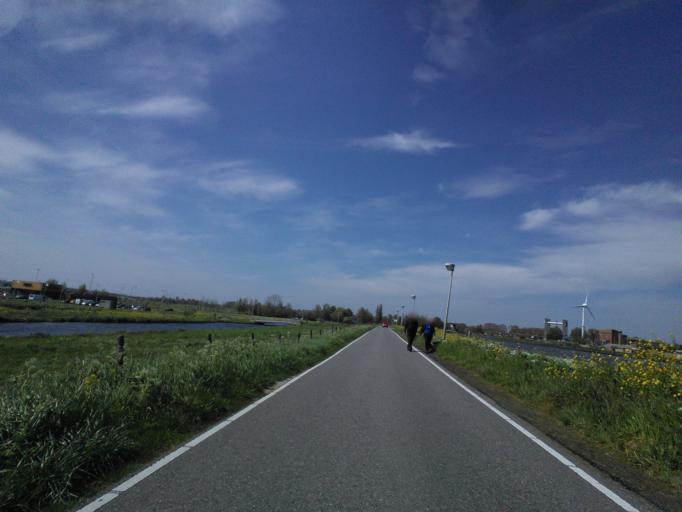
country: NL
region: South Holland
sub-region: Gemeente Gouda
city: Bloemendaal
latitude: 52.0092
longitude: 4.6887
